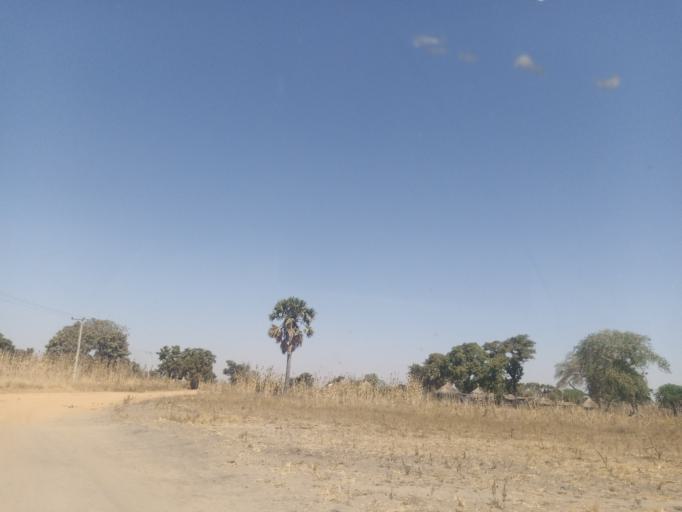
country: NG
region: Adamawa
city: Yola
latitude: 9.2889
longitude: 12.8850
